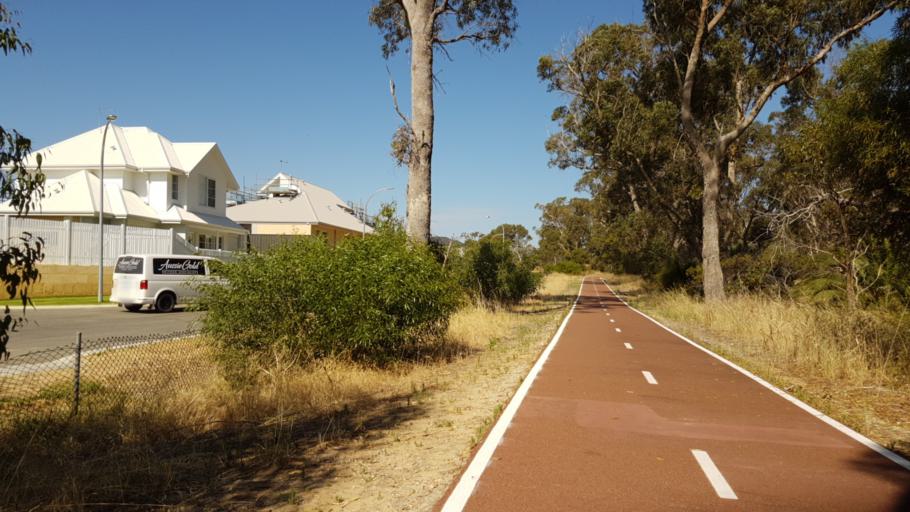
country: AU
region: Western Australia
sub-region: Stirling
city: Karrinyup
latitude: -31.8563
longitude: 115.7944
